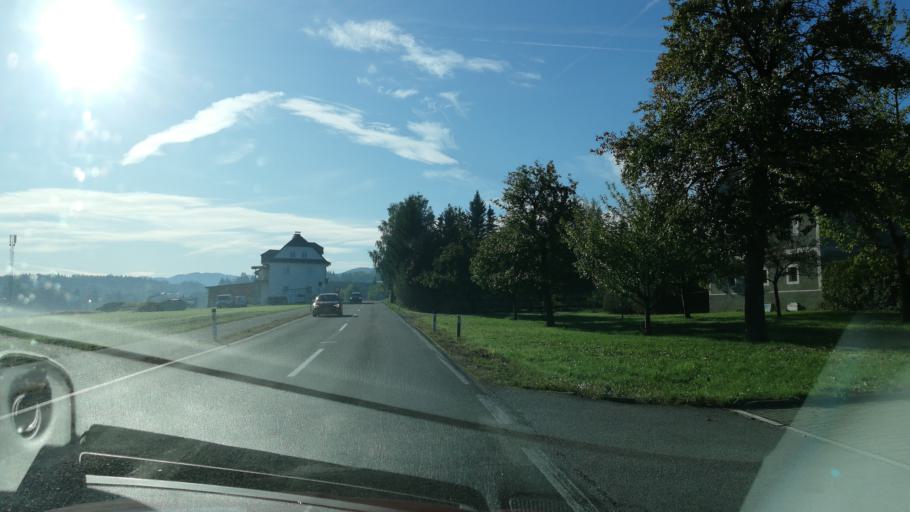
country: AT
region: Upper Austria
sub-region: Politischer Bezirk Steyr-Land
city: Waldneukirchen
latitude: 48.0099
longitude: 14.2467
